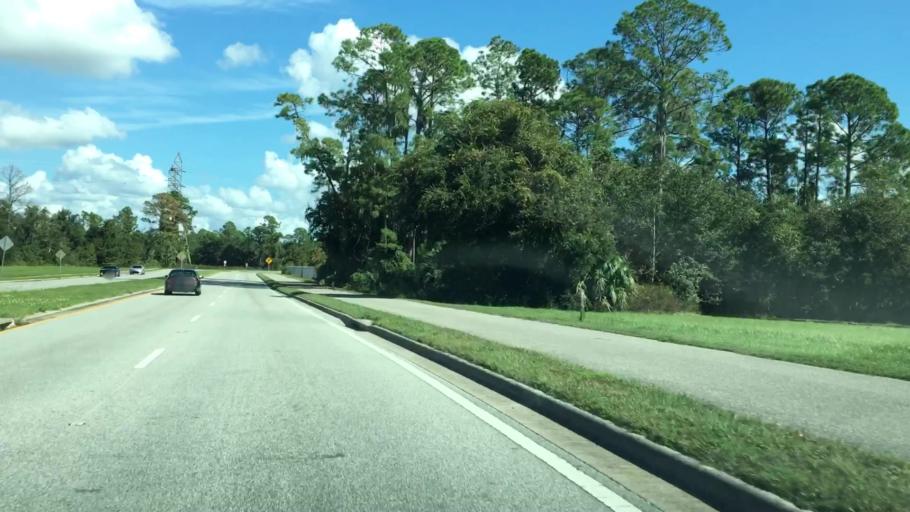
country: US
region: Florida
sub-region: Volusia County
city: Deltona
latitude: 28.8724
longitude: -81.2755
